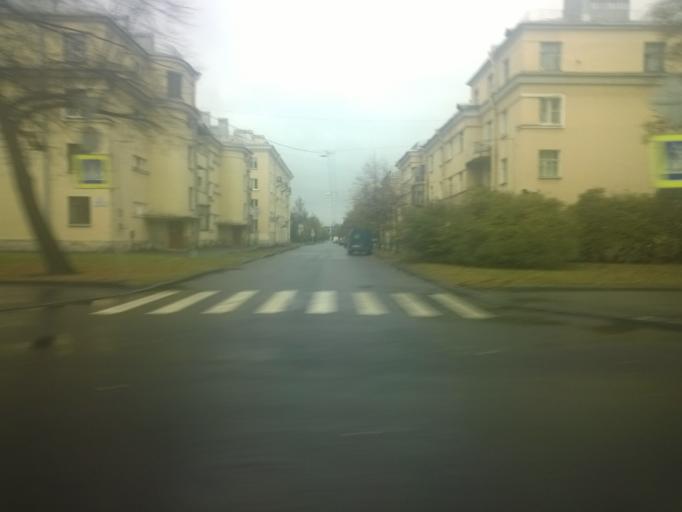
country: RU
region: St.-Petersburg
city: Avtovo
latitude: 59.8886
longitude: 30.2695
